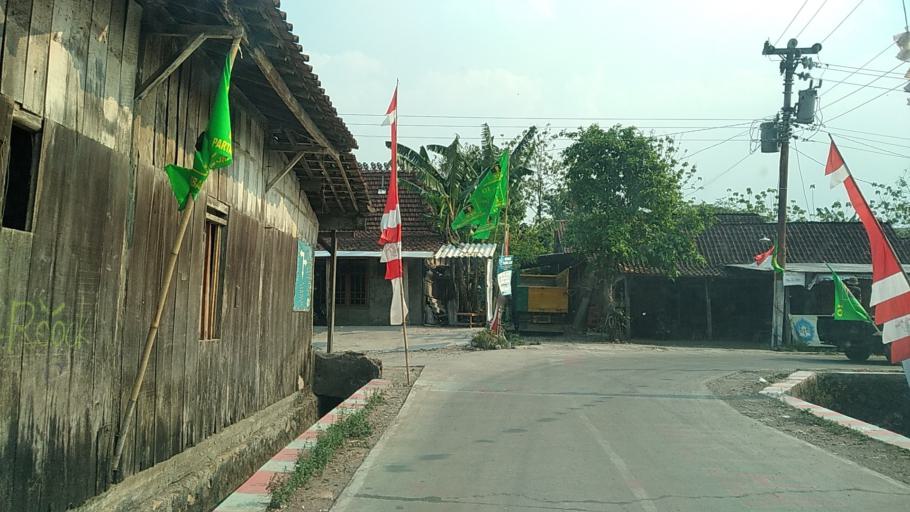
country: ID
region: Central Java
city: Mranggen
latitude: -7.0784
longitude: 110.4668
